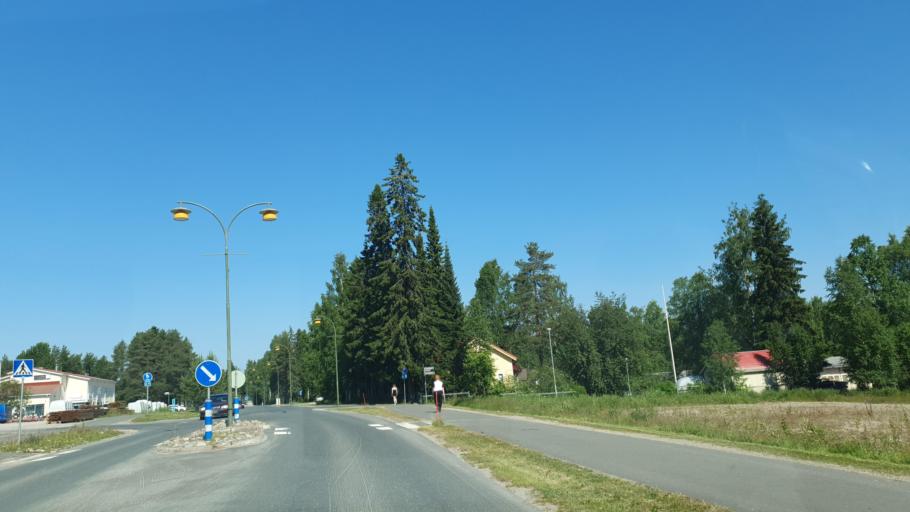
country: FI
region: Lapland
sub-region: Rovaniemi
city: Ranua
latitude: 65.9288
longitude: 26.5178
